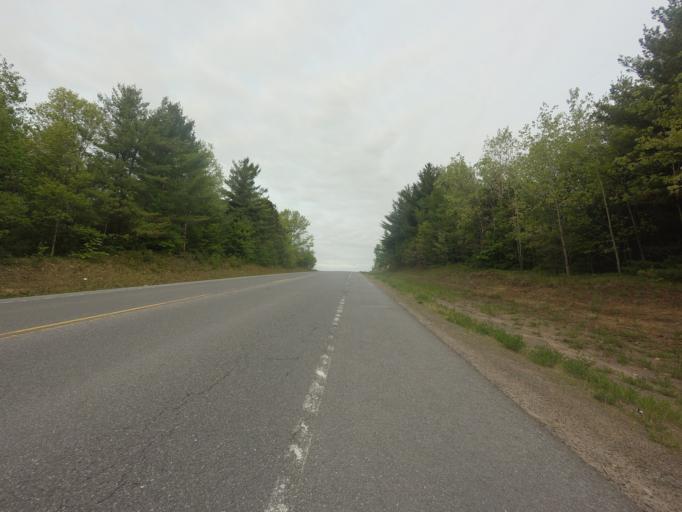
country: US
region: New York
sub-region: Jefferson County
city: Carthage
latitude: 44.0340
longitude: -75.6296
